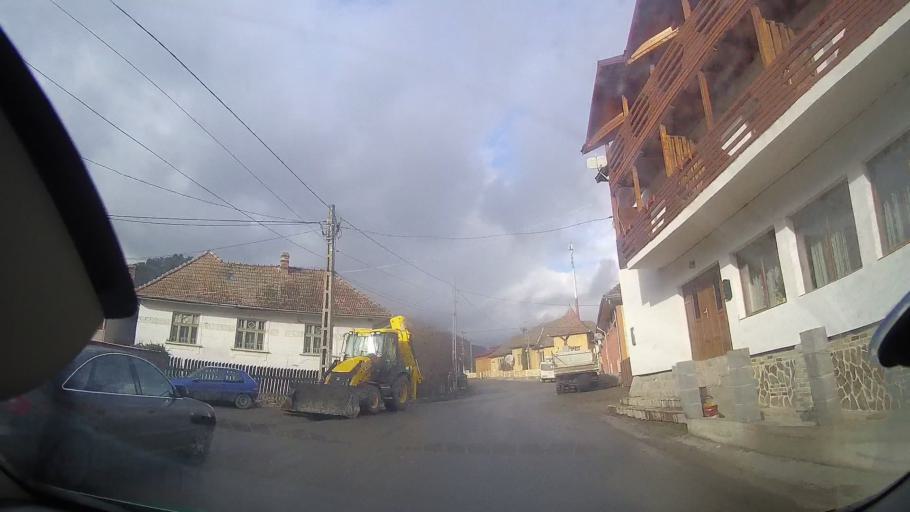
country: RO
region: Alba
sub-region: Comuna Ocolis
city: Ocolis
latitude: 46.4783
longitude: 23.4658
